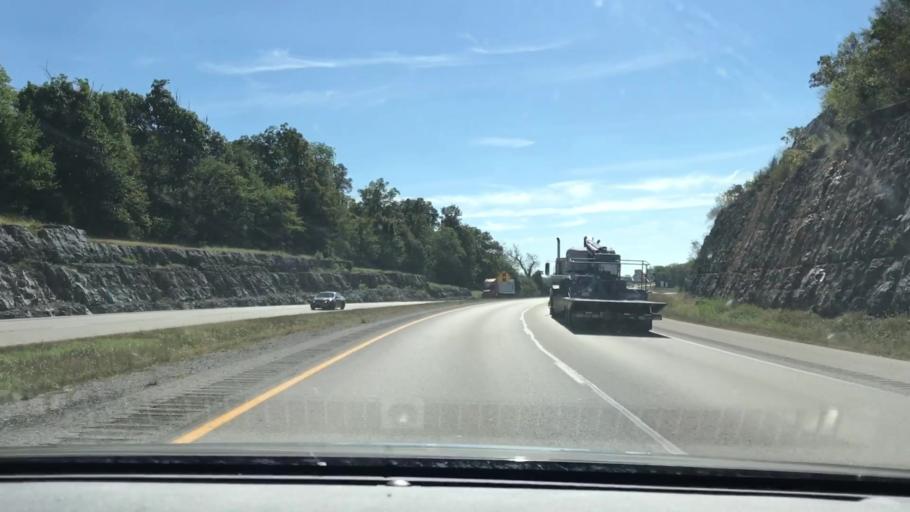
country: US
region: Kentucky
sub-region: Logan County
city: Russellville
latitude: 36.8333
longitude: -86.9093
